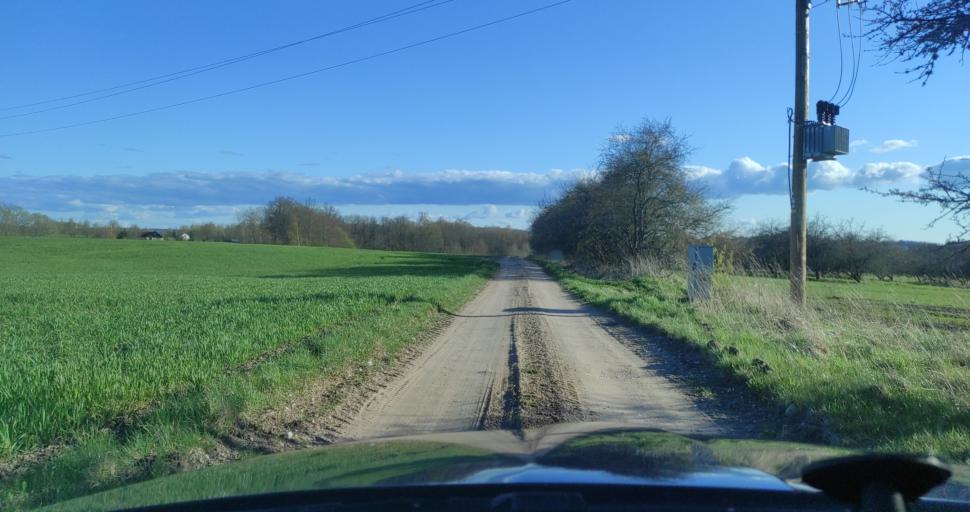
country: LV
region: Kuldigas Rajons
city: Kuldiga
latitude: 56.8770
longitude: 21.8342
